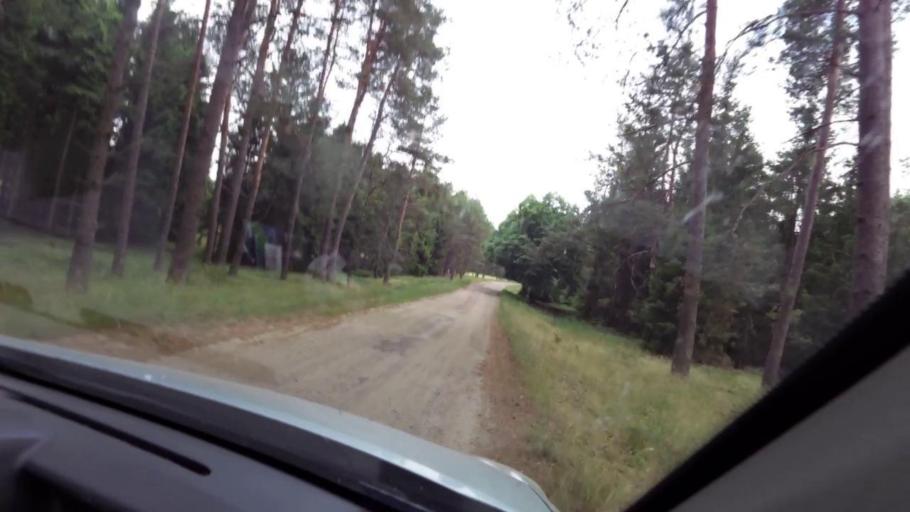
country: PL
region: Pomeranian Voivodeship
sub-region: Powiat bytowski
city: Trzebielino
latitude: 54.2032
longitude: 17.0077
